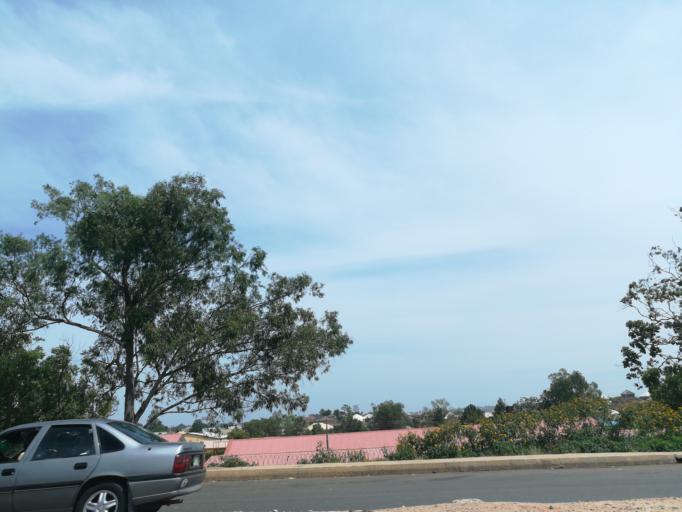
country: NG
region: Plateau
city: Bukuru
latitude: 9.8398
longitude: 8.8659
